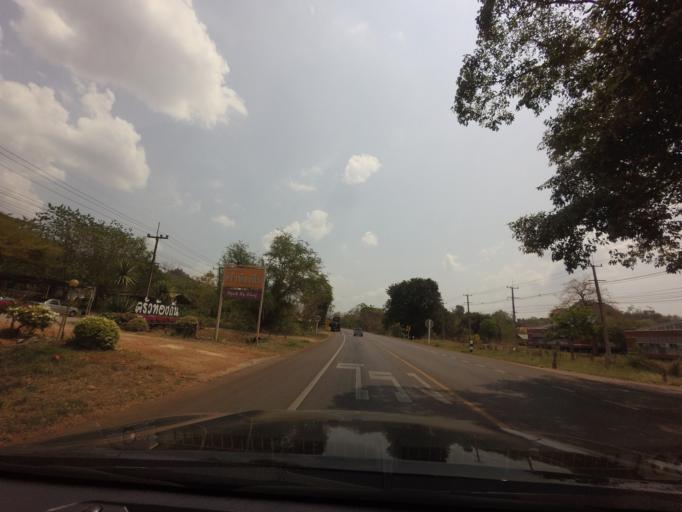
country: TH
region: Kanchanaburi
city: Sai Yok
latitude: 14.1370
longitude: 99.1509
